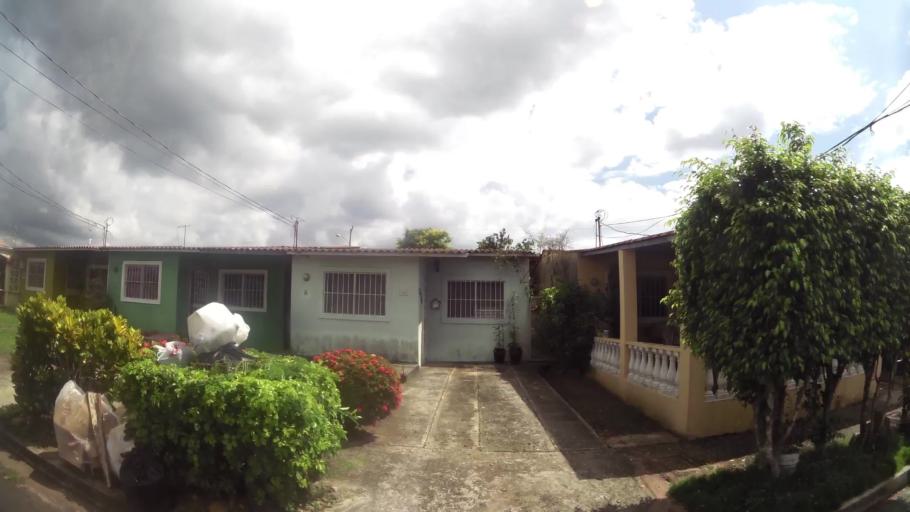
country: PA
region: Panama
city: Nuevo Arraijan
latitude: 8.9300
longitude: -79.7279
